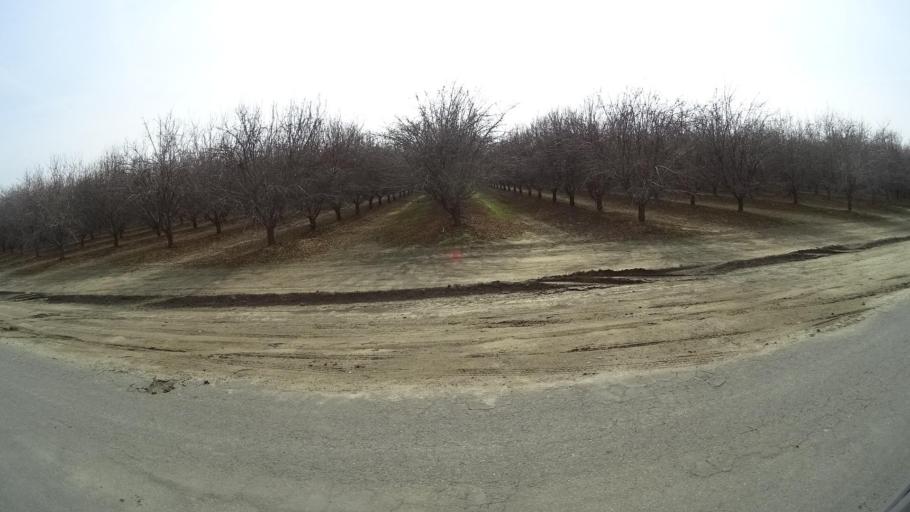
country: US
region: California
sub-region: Kern County
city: Arvin
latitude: 35.1798
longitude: -118.8723
